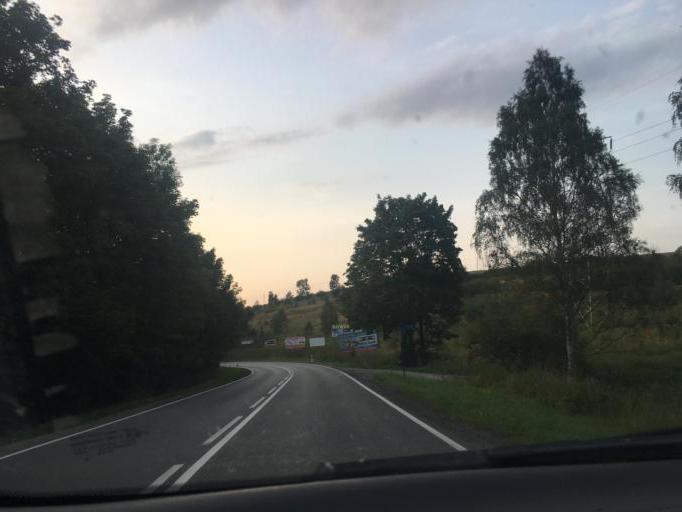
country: PL
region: Lower Silesian Voivodeship
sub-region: Powiat klodzki
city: Nowa Ruda
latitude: 50.5709
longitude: 16.5324
